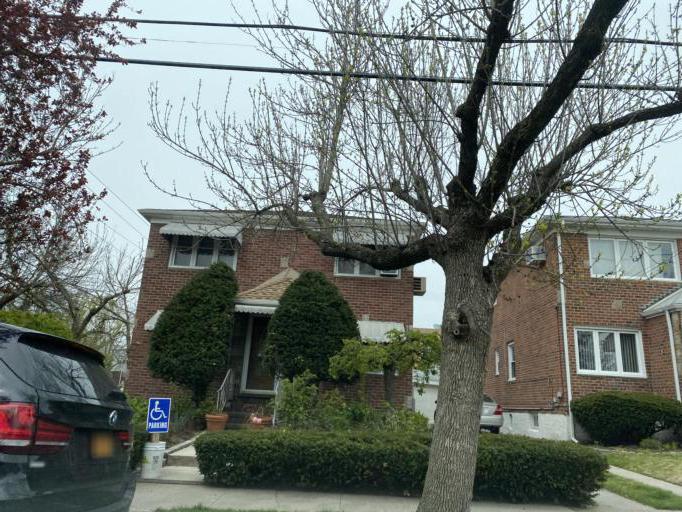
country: US
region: New York
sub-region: Queens County
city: Borough of Queens
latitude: 40.6695
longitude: -73.8258
